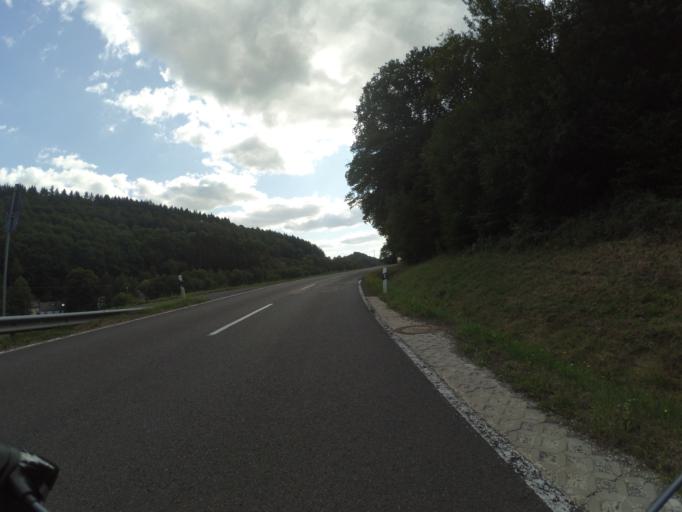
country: DE
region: Rheinland-Pfalz
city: Budlich
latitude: 49.7805
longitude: 6.8955
